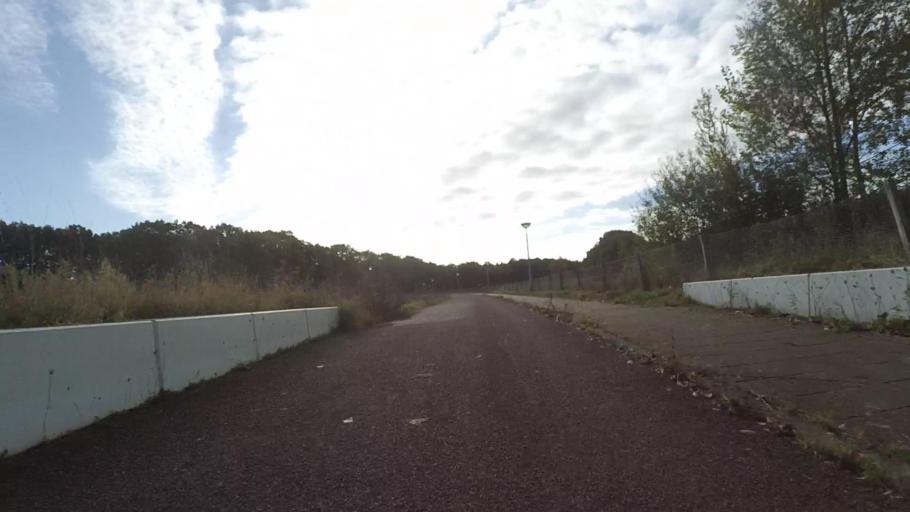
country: NL
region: Gelderland
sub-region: Gemeente Ermelo
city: Horst
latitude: 52.3217
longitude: 5.5931
